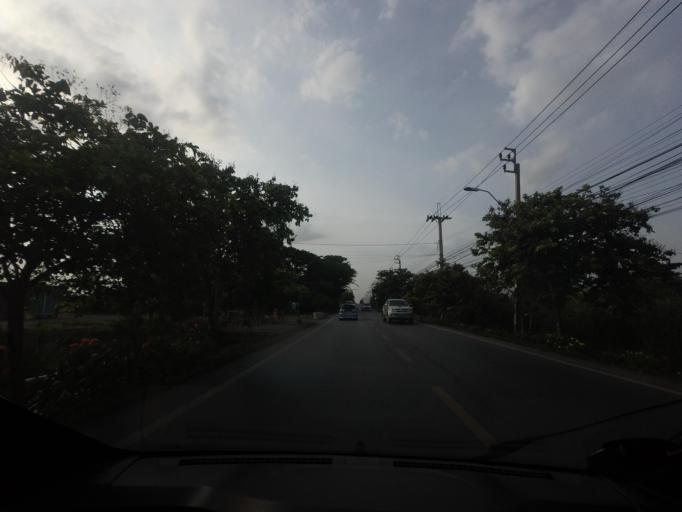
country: TH
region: Bangkok
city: Nong Chok
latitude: 13.8274
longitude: 100.8704
